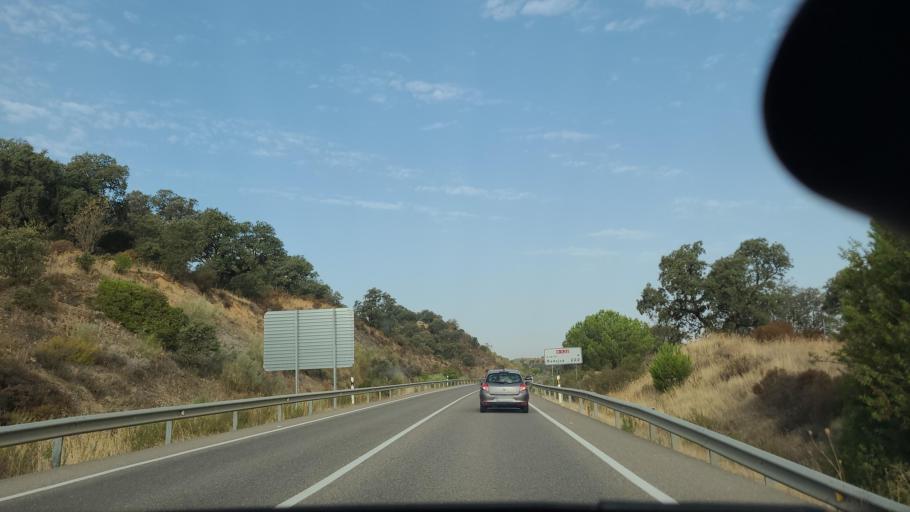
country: ES
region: Andalusia
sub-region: Province of Cordoba
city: Espiel
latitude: 38.1732
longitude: -5.0041
